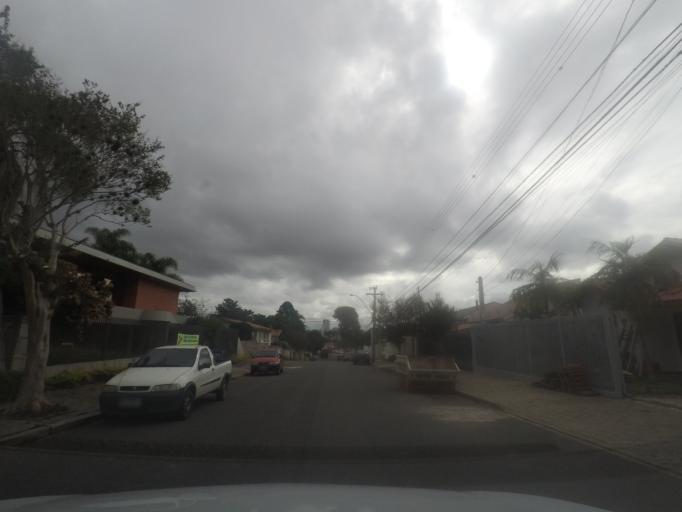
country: BR
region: Parana
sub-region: Curitiba
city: Curitiba
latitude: -25.4417
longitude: -49.2459
